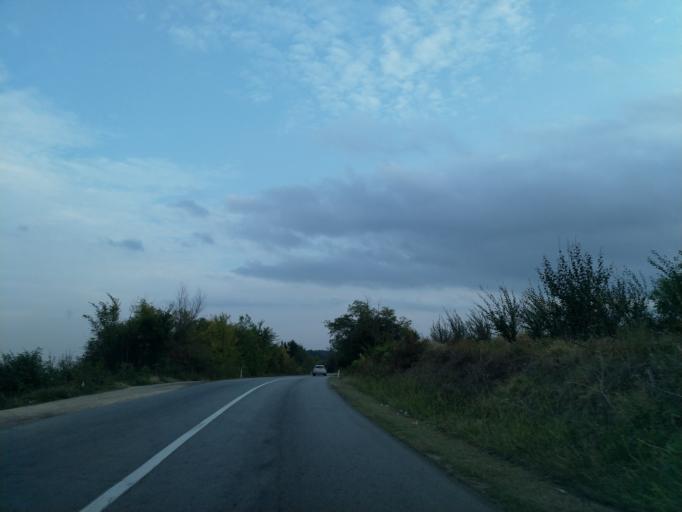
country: RS
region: Central Serbia
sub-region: Sumadijski Okrug
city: Topola
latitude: 44.1559
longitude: 20.7396
